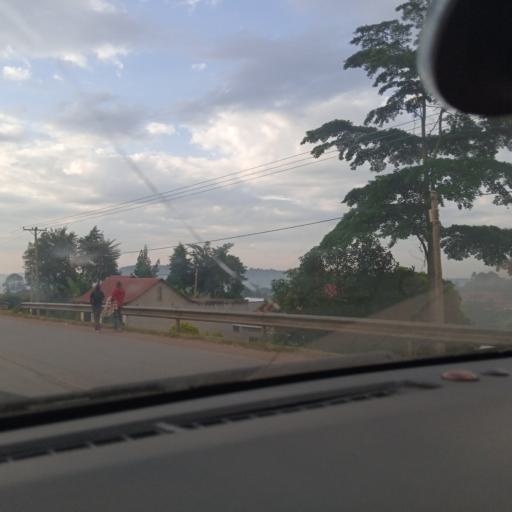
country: UG
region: Central Region
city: Masaka
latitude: -0.3387
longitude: 31.7020
